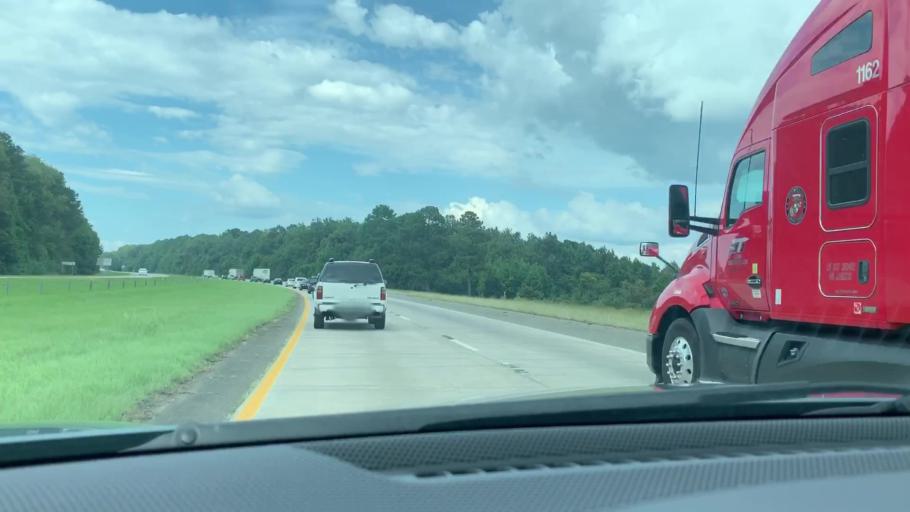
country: US
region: South Carolina
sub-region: Hampton County
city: Yemassee
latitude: 32.6337
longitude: -80.8812
